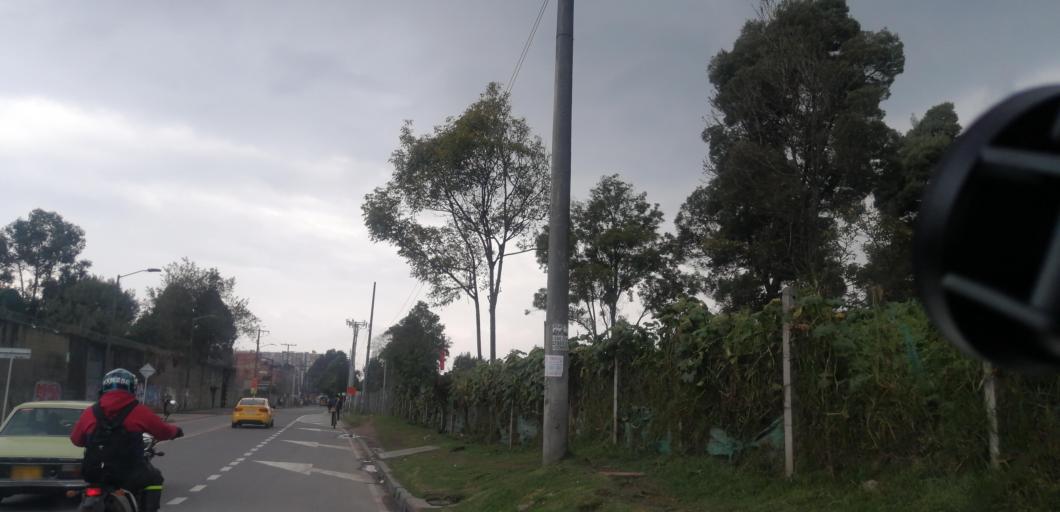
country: CO
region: Cundinamarca
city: Funza
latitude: 4.6865
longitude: -74.1510
